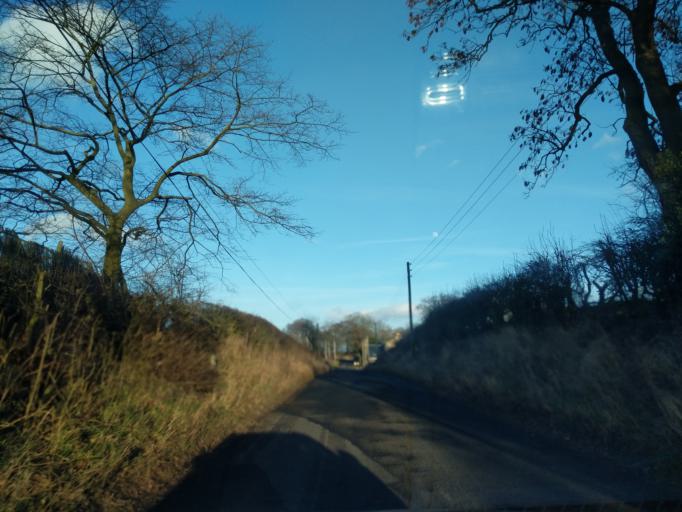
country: GB
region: Scotland
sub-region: Edinburgh
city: Balerno
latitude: 55.9034
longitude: -3.3297
